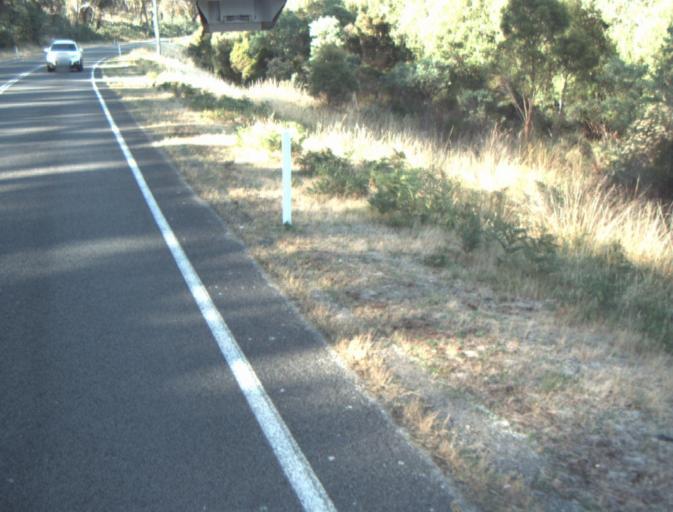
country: AU
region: Tasmania
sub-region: Launceston
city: Newstead
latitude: -41.4251
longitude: 147.2552
